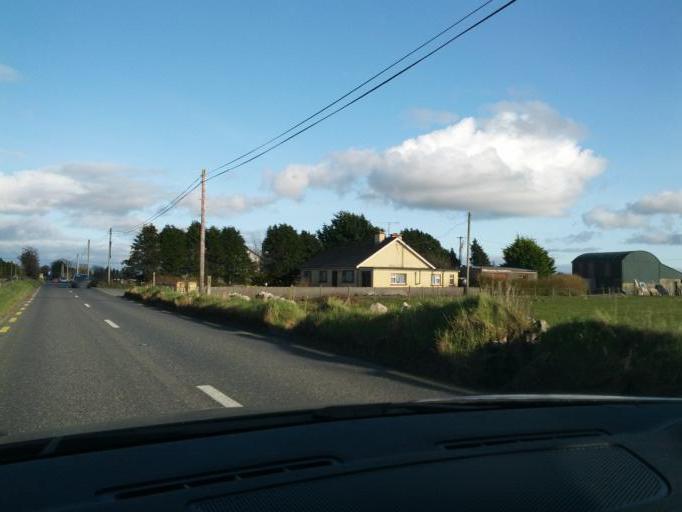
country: IE
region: Connaught
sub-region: Roscommon
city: Roscommon
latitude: 53.6501
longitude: -8.2341
